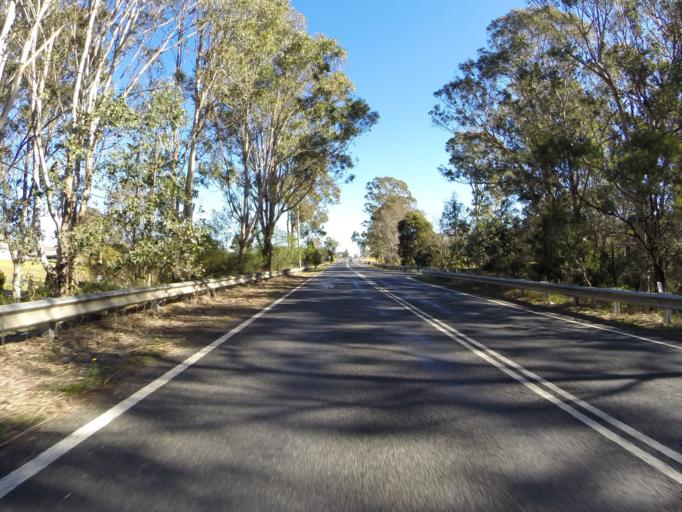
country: AU
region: New South Wales
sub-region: Wollondilly
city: Douglas Park
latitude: -34.2412
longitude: 150.7020
